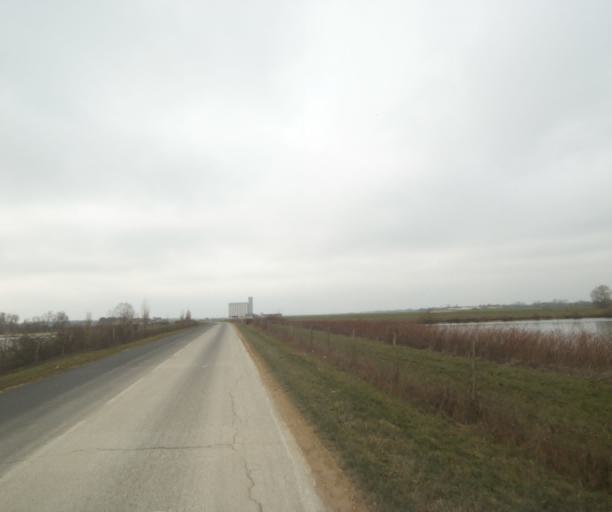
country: FR
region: Champagne-Ardenne
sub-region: Departement de la Haute-Marne
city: Villiers-en-Lieu
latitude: 48.6528
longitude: 4.7757
